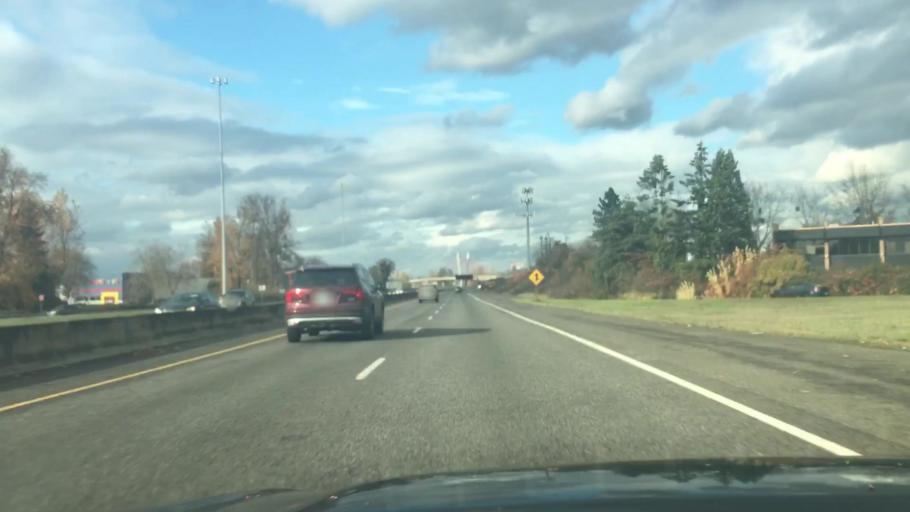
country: US
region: Oregon
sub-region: Lane County
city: Eugene
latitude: 44.0710
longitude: -123.1023
